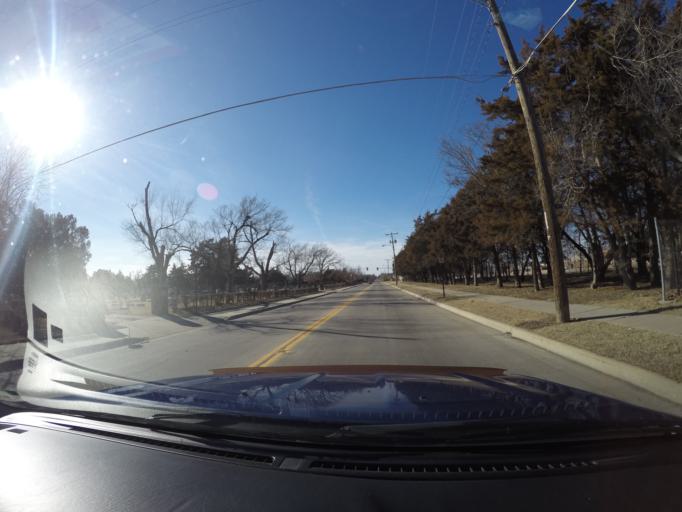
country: US
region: Kansas
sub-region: Harvey County
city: Newton
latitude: 38.0428
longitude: -97.3275
